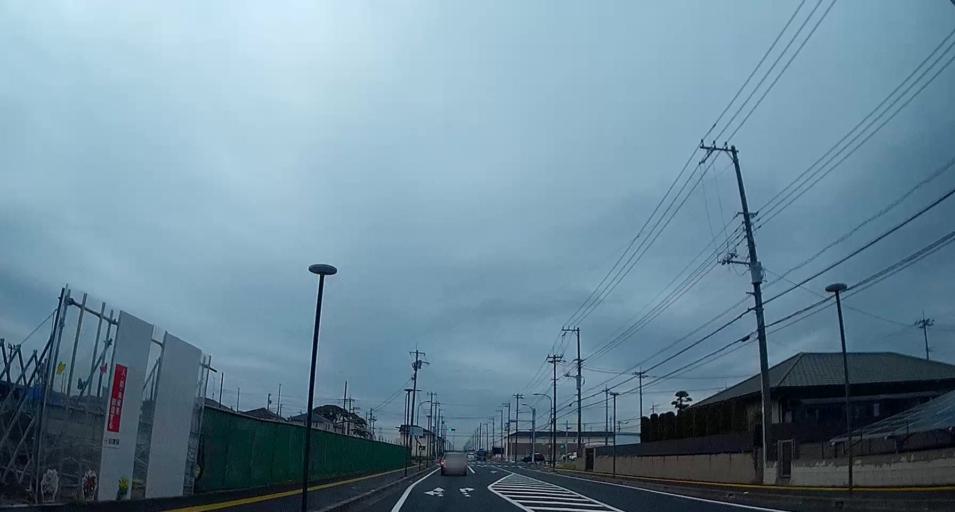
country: JP
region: Chiba
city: Kisarazu
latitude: 35.4330
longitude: 139.9549
